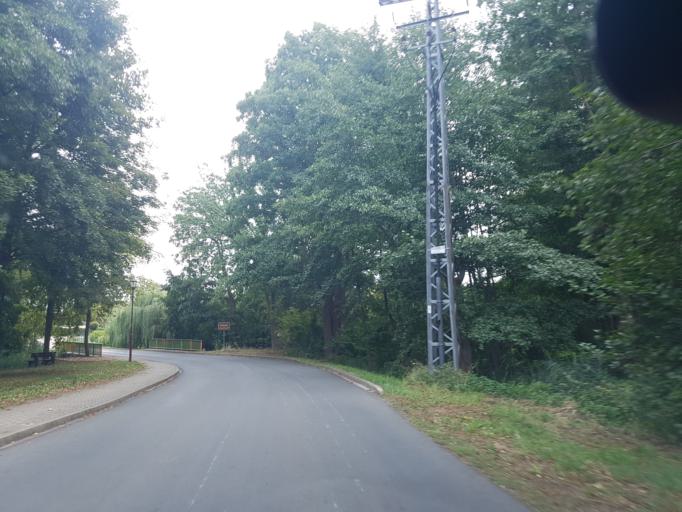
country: DE
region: Saxony-Anhalt
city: Klieken
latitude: 51.9550
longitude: 12.3064
